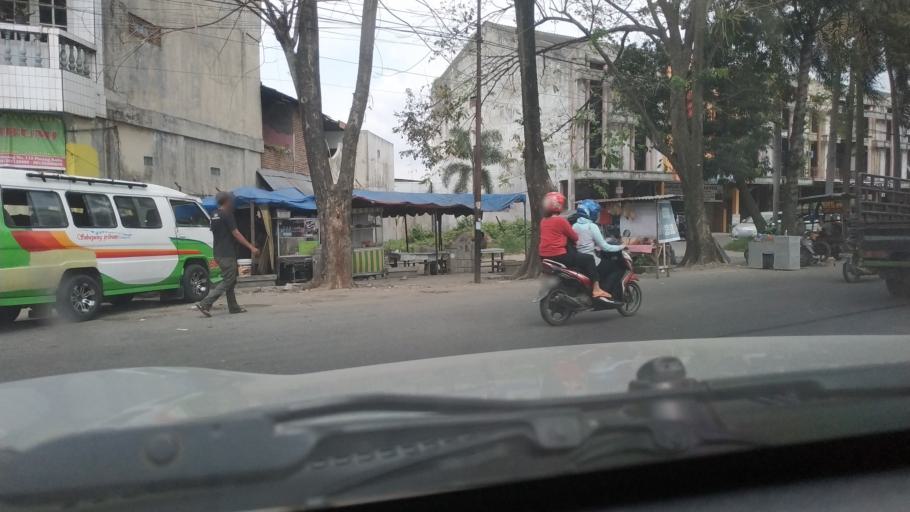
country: ID
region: North Sumatra
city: Sunggal
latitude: 3.5890
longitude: 98.6110
